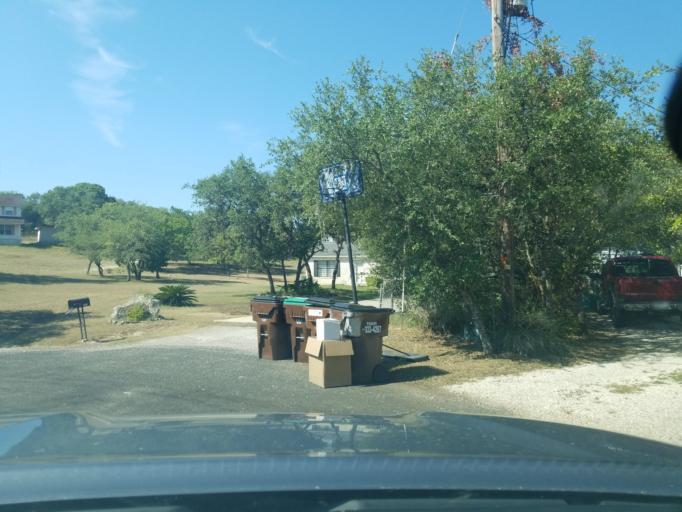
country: US
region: Texas
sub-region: Bexar County
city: Timberwood Park
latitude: 29.6777
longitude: -98.5138
